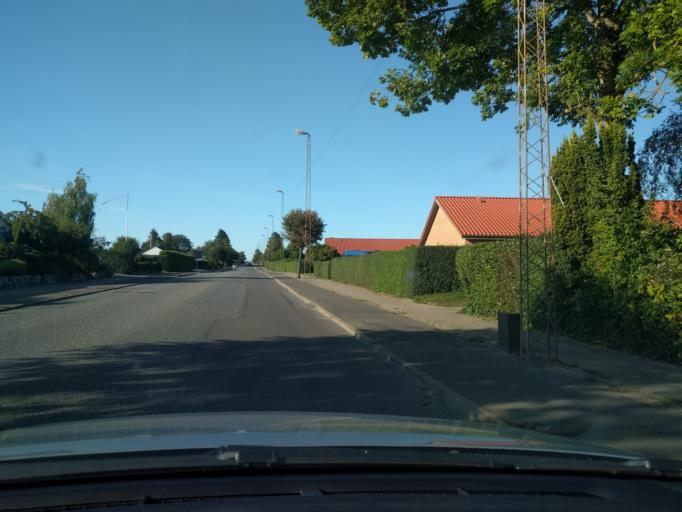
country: DK
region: Central Jutland
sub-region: Horsens Kommune
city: Horsens
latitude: 55.8641
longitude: 9.9162
